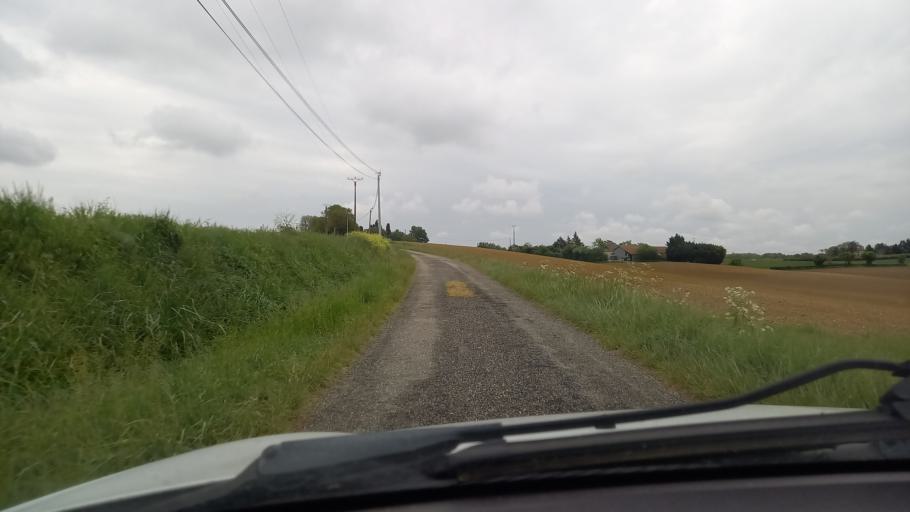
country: FR
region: Midi-Pyrenees
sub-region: Departement du Gers
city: Aubiet
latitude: 43.7589
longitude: 0.8454
